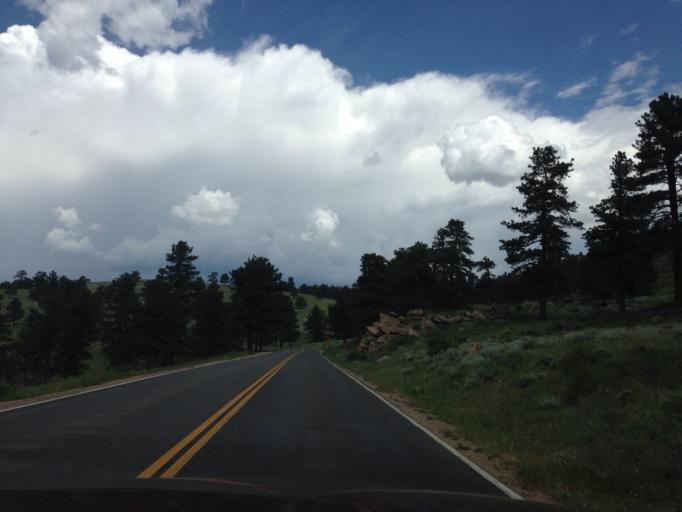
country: US
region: Colorado
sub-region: Larimer County
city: Estes Park
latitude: 40.3802
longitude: -105.5997
